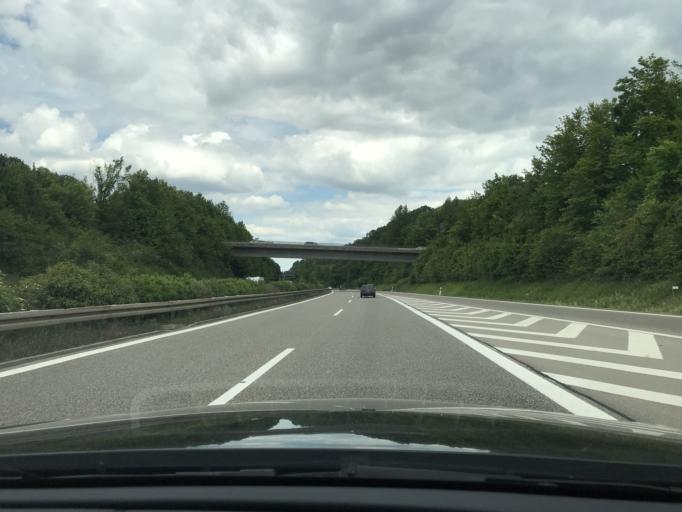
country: DE
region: Baden-Wuerttemberg
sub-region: Regierungsbezirk Stuttgart
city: Korb
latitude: 48.8601
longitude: 9.3629
